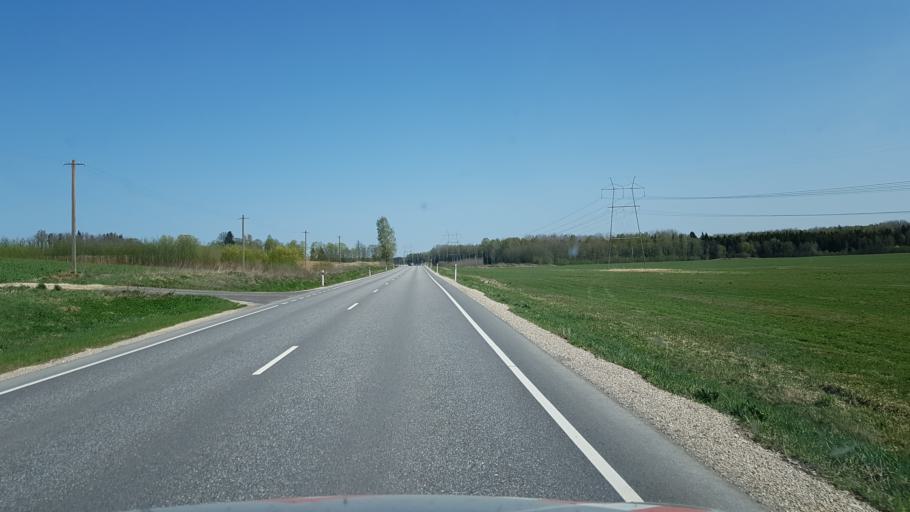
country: EE
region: Viljandimaa
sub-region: Abja vald
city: Abja-Paluoja
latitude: 58.2857
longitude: 25.2908
